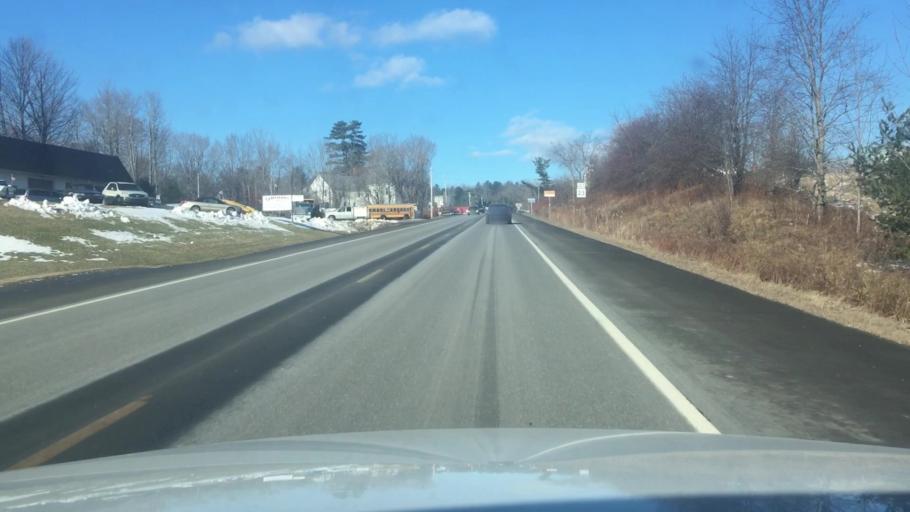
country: US
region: Maine
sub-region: Kennebec County
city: Waterville
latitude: 44.6045
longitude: -69.6604
